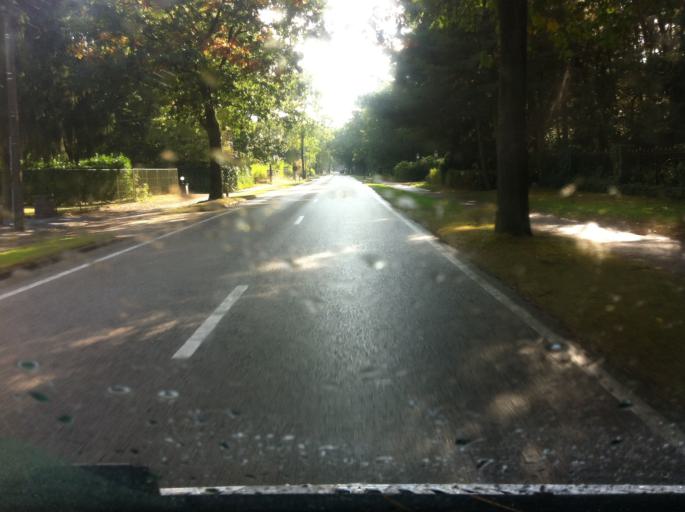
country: BE
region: Flanders
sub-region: Provincie Limburg
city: Maasmechelen
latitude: 50.9774
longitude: 5.6632
